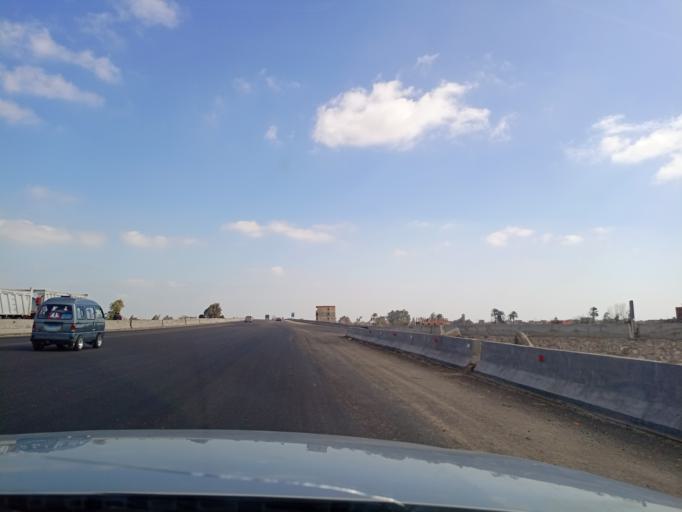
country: EG
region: Muhafazat al Minufiyah
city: Al Bajur
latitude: 30.4061
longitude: 31.0434
